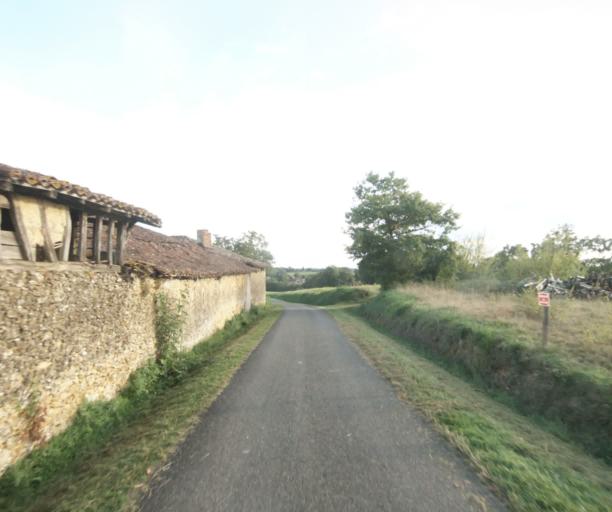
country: FR
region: Midi-Pyrenees
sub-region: Departement du Gers
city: Le Houga
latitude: 43.8489
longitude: -0.1265
